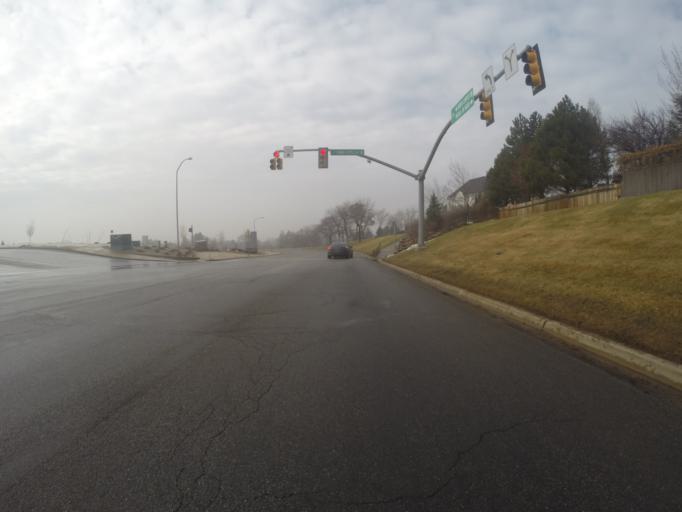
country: US
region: Utah
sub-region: Salt Lake County
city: Salt Lake City
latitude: 40.7730
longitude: -111.8405
